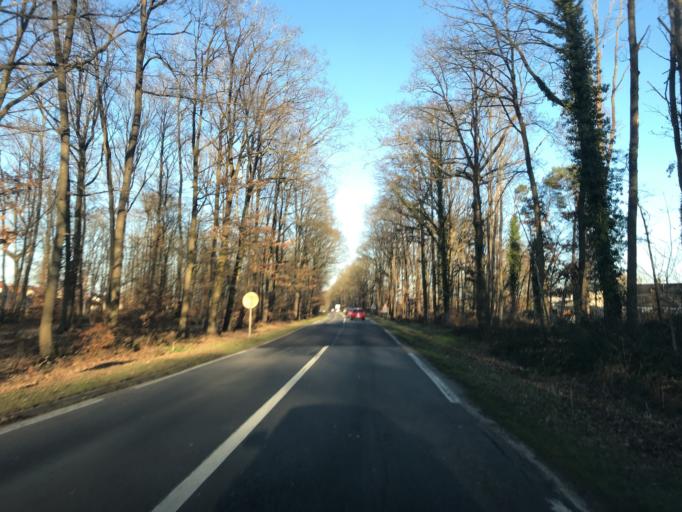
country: FR
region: Haute-Normandie
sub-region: Departement de l'Eure
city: Saint-Sebastien-de-Morsent
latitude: 49.0094
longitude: 1.0951
